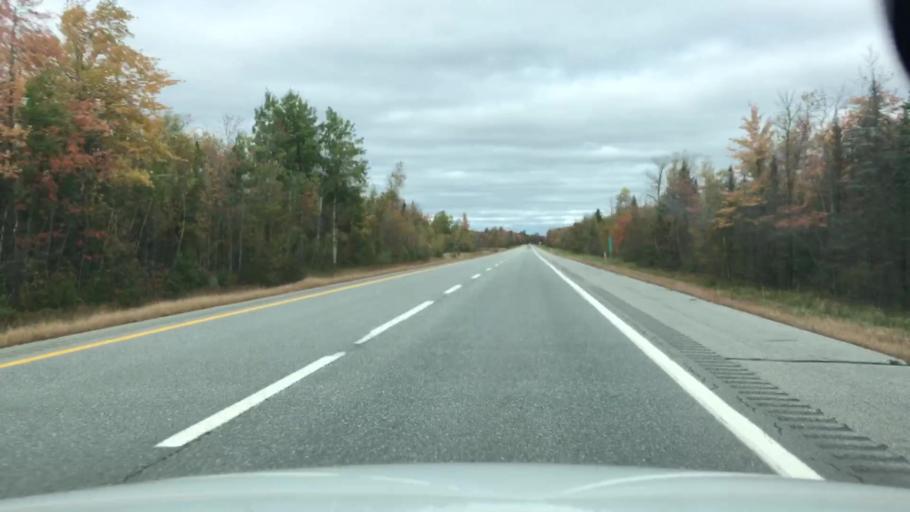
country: US
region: Maine
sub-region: Waldo County
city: Burnham
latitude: 44.6836
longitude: -69.4760
